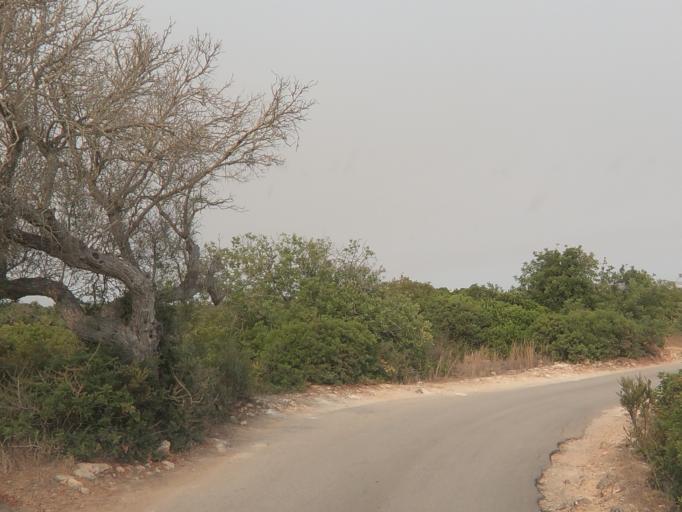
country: PT
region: Faro
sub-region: Silves
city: Armacao de Pera
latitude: 37.0960
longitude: -8.4036
